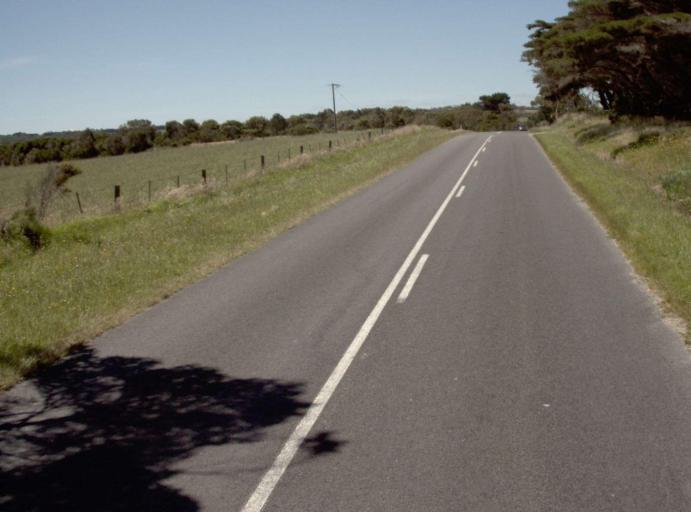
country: AU
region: Victoria
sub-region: Bass Coast
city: North Wonthaggi
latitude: -38.7974
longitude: 146.0865
